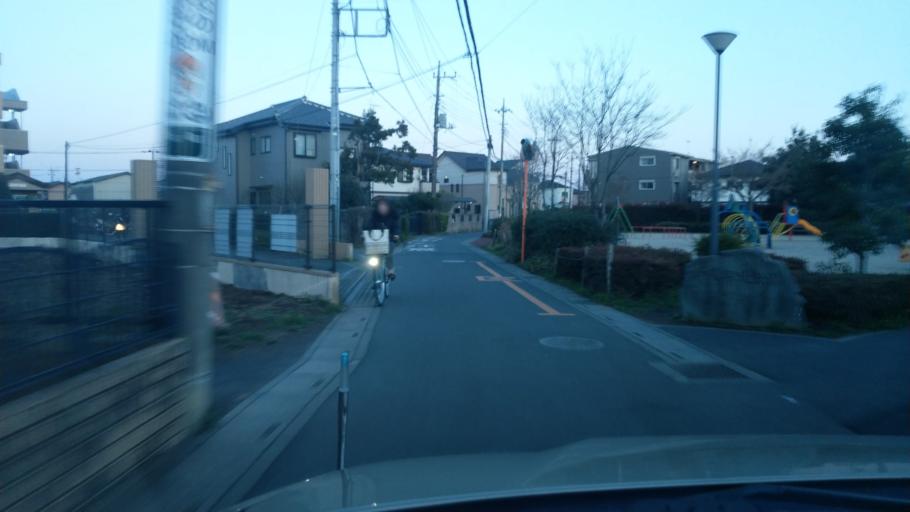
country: JP
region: Saitama
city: Yono
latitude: 35.9183
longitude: 139.5825
